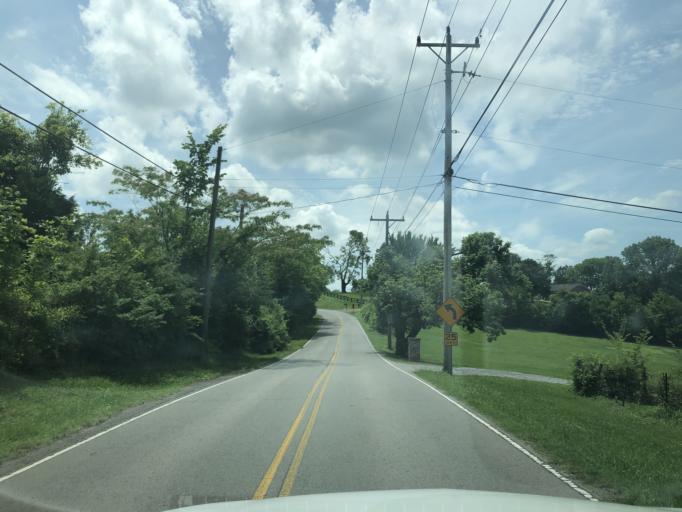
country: US
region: Tennessee
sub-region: Rutherford County
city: La Vergne
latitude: 36.0252
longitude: -86.6464
